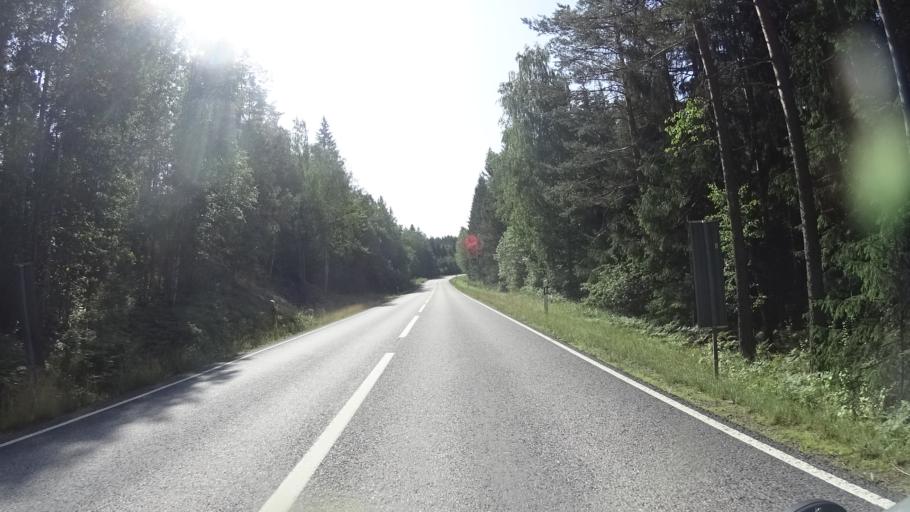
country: SE
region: Kalmar
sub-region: Vasterviks Kommun
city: Overum
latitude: 58.0740
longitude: 16.1928
